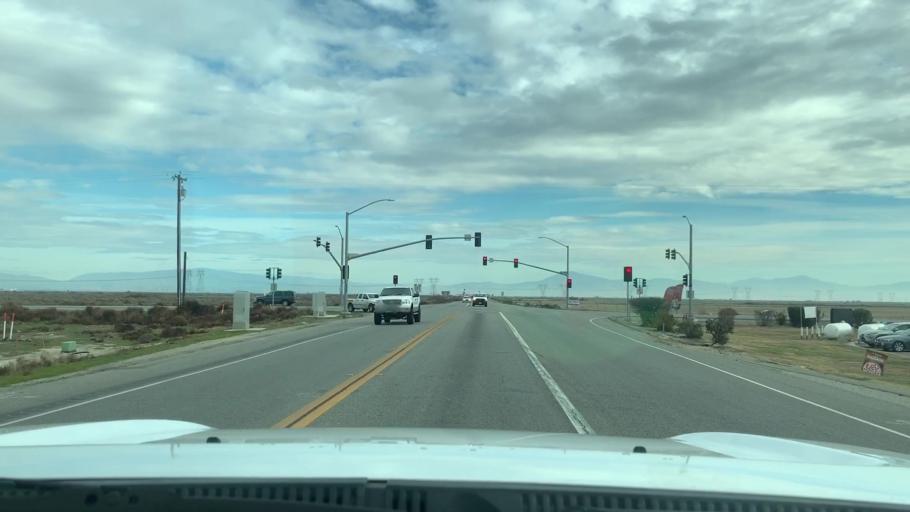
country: US
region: California
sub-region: Kern County
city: Rosedale
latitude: 35.2674
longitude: -119.2536
